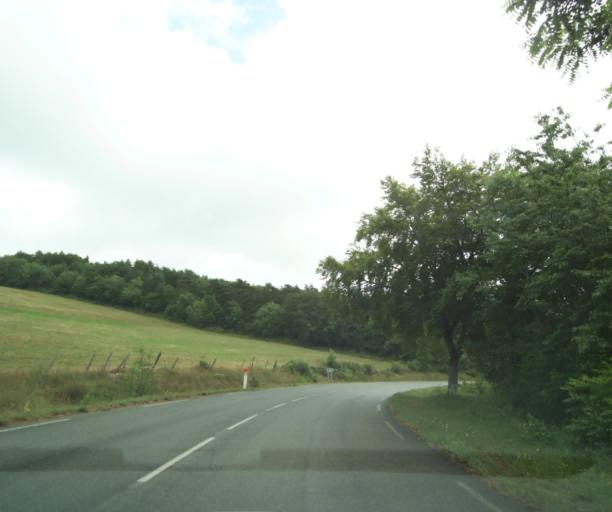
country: FR
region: Languedoc-Roussillon
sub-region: Departement de la Lozere
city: La Canourgue
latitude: 44.4101
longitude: 3.1487
